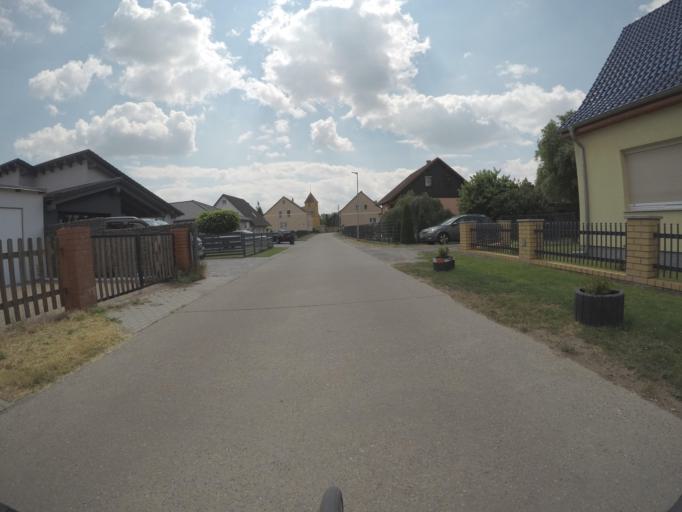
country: DE
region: Brandenburg
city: Roskow
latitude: 52.4447
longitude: 12.6605
